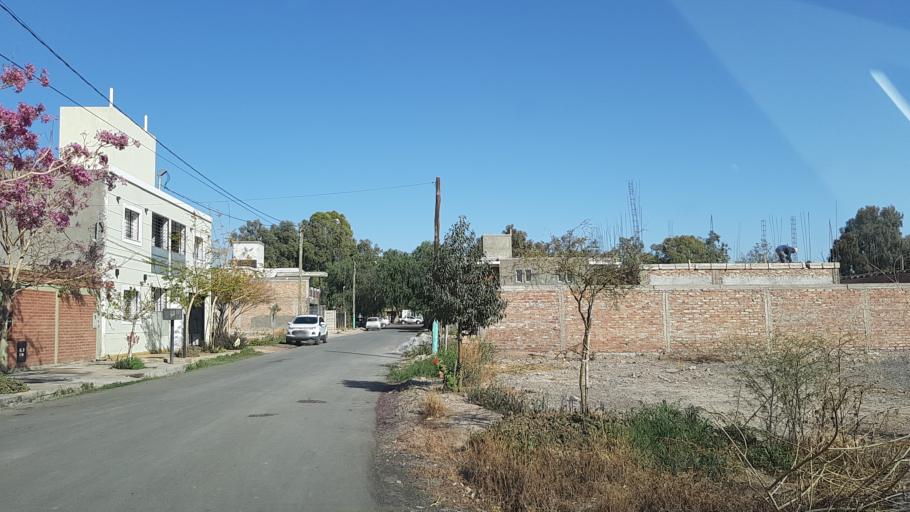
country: AR
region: San Juan
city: San Juan
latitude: -31.5452
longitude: -68.5783
